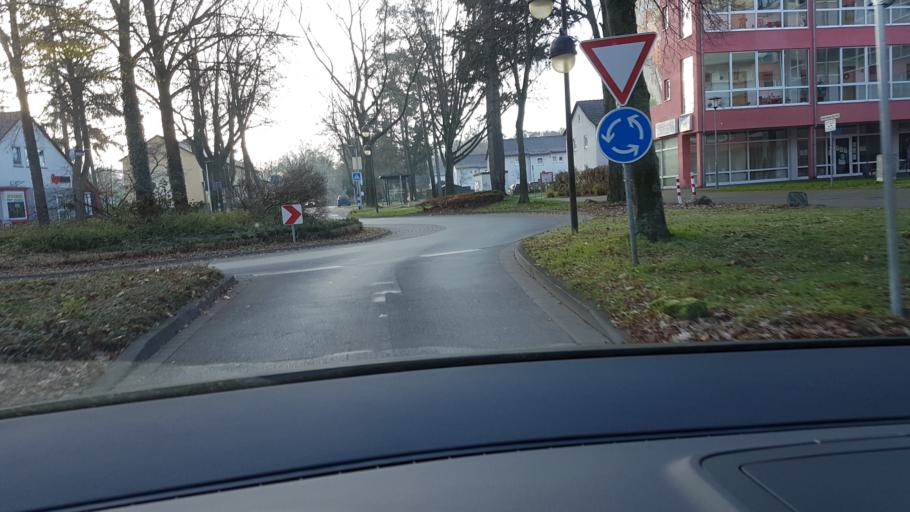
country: DE
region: North Rhine-Westphalia
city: Espelkamp
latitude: 52.3777
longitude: 8.6219
